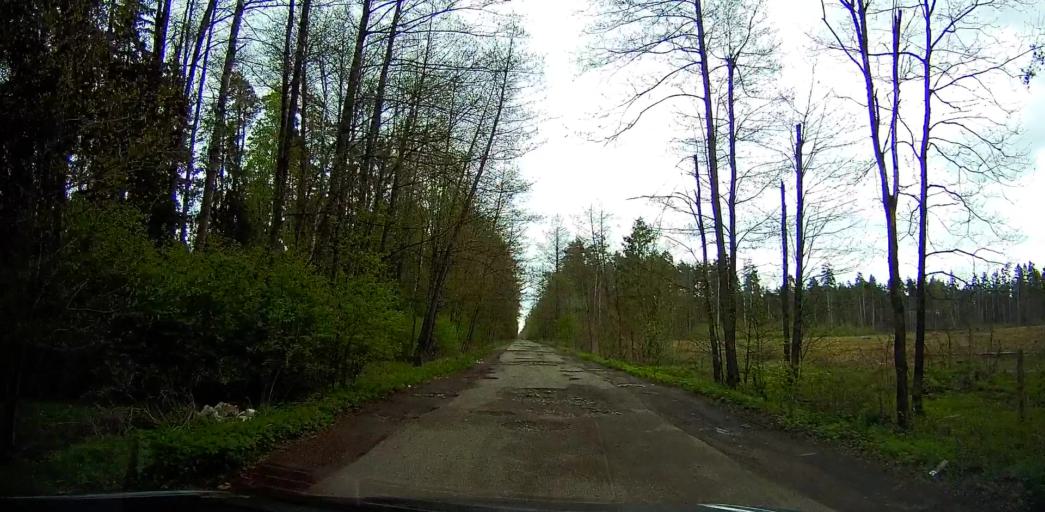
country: RU
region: Moskovskaya
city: Malyshevo
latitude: 55.5527
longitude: 38.3451
